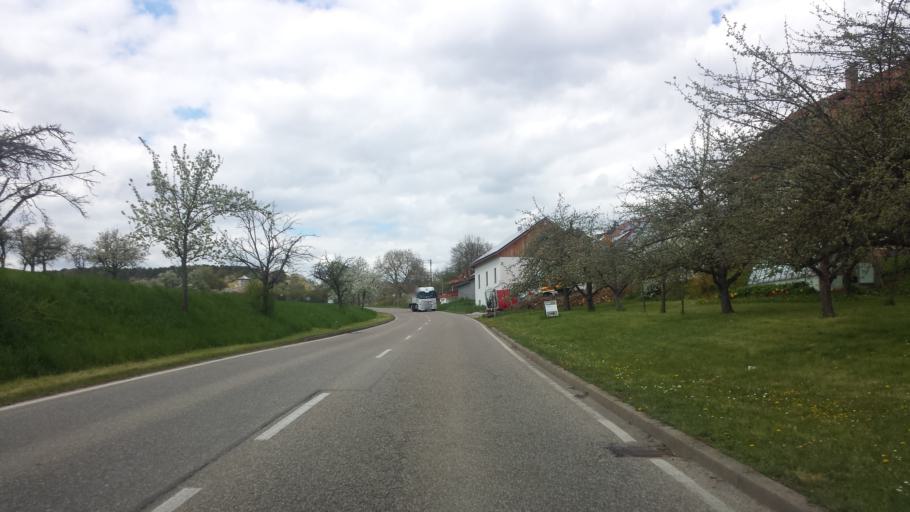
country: DE
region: Baden-Wuerttemberg
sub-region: Regierungsbezirk Stuttgart
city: Weissach
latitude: 48.8494
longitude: 8.9206
